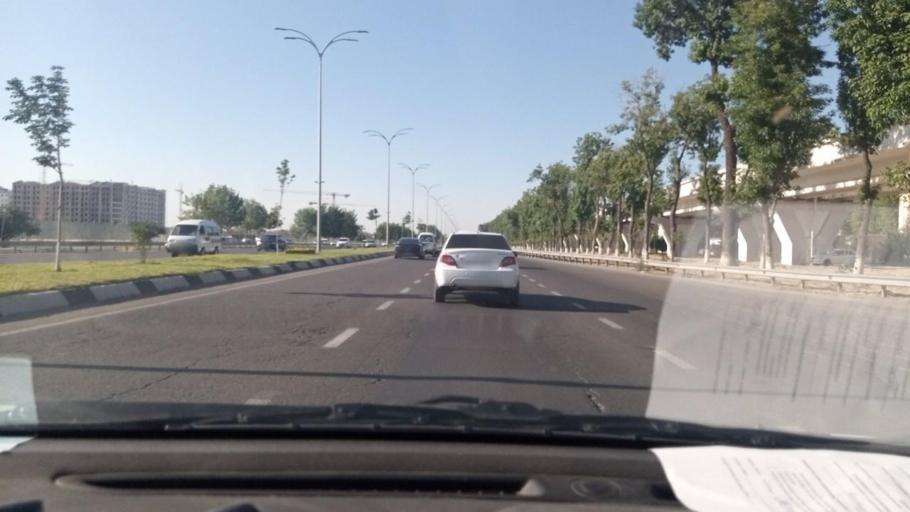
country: UZ
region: Toshkent Shahri
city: Bektemir
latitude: 41.2805
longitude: 69.3609
